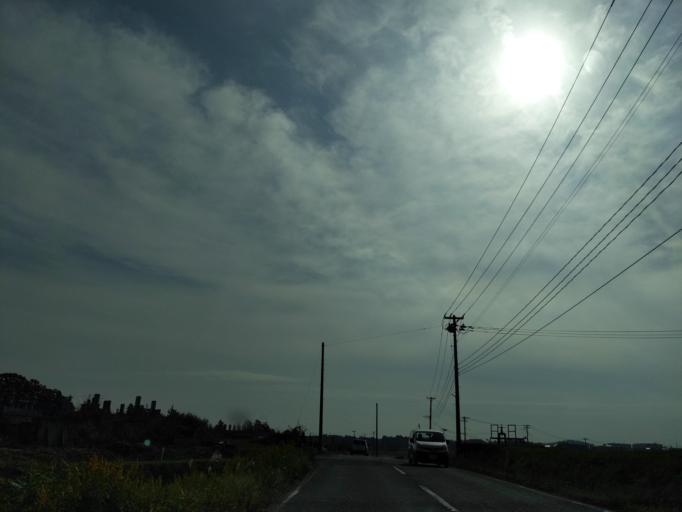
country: JP
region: Fukushima
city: Koriyama
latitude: 37.4325
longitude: 140.3140
